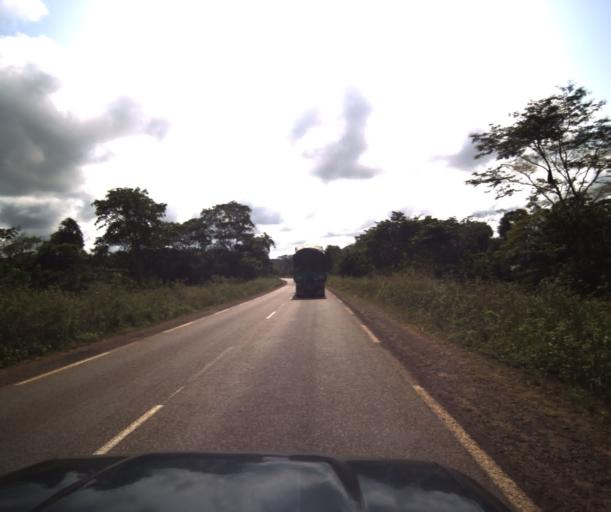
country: CM
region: Littoral
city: Edea
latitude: 3.8027
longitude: 10.2401
